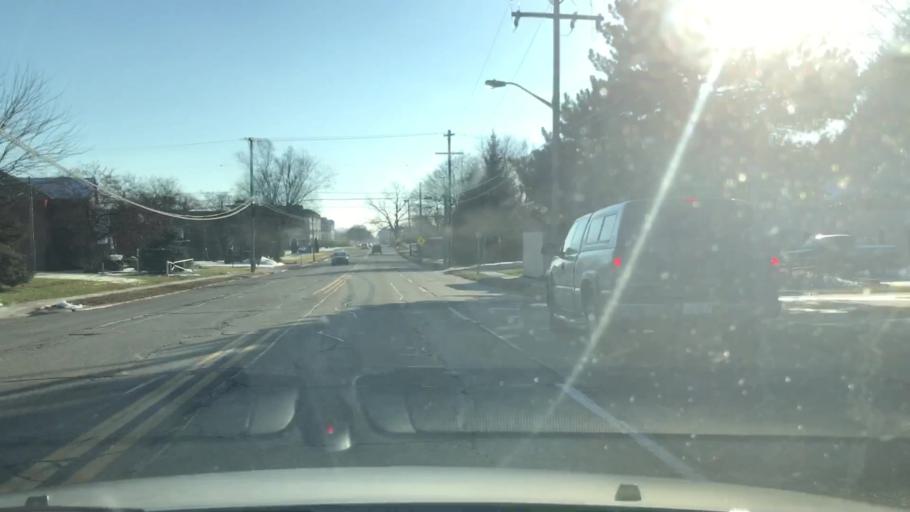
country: US
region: Michigan
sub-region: Oakland County
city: Clawson
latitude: 42.5240
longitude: -83.1383
